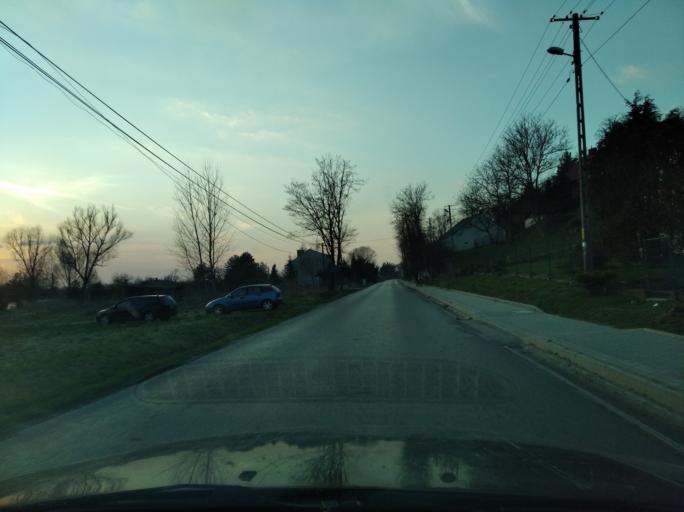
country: PL
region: Subcarpathian Voivodeship
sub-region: Powiat przeworski
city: Przeworsk
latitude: 50.0393
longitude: 22.5085
